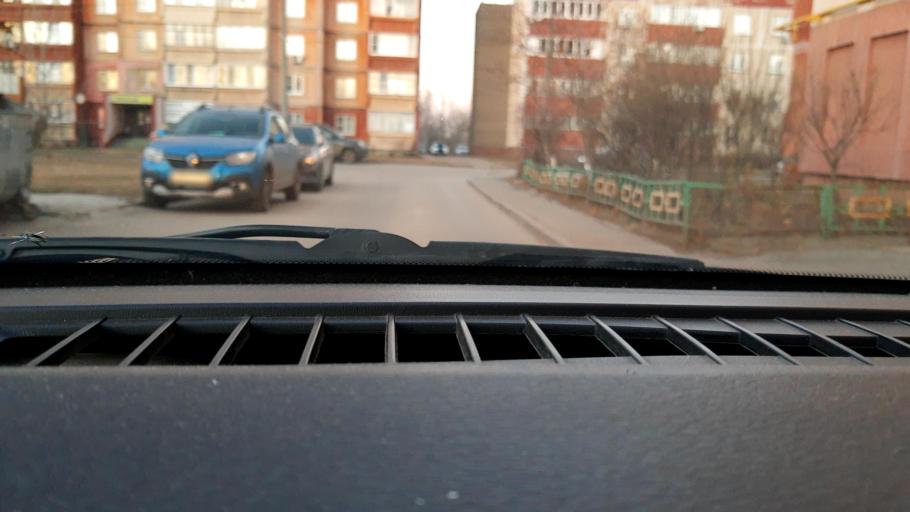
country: RU
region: Nizjnij Novgorod
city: Gorbatovka
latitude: 56.2391
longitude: 43.8259
